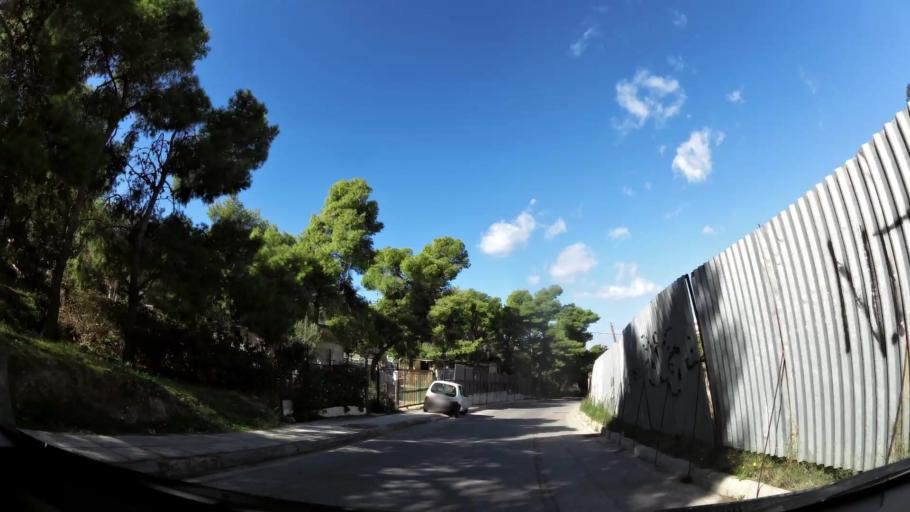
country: GR
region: Attica
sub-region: Nomarchia Anatolikis Attikis
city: Vouliagmeni
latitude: 37.8260
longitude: 23.7813
